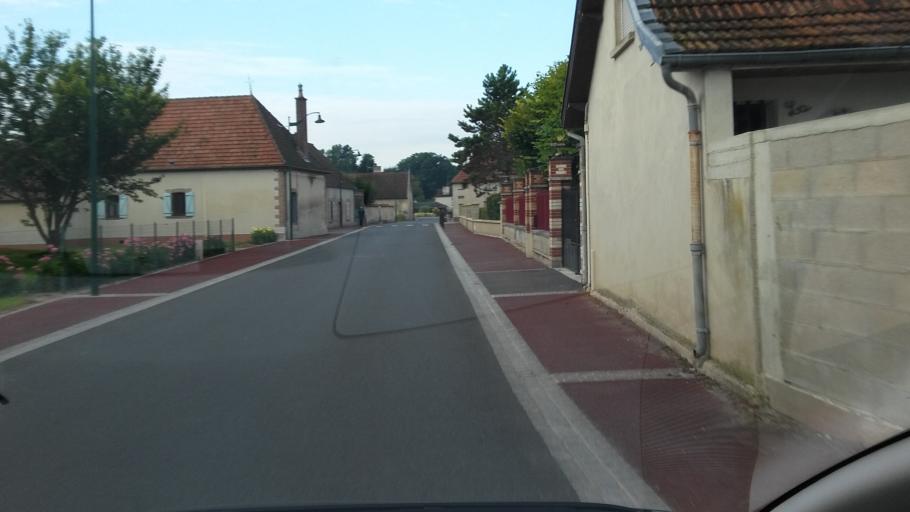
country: FR
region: Champagne-Ardenne
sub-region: Departement de la Marne
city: Connantre
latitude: 48.7267
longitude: 3.9234
